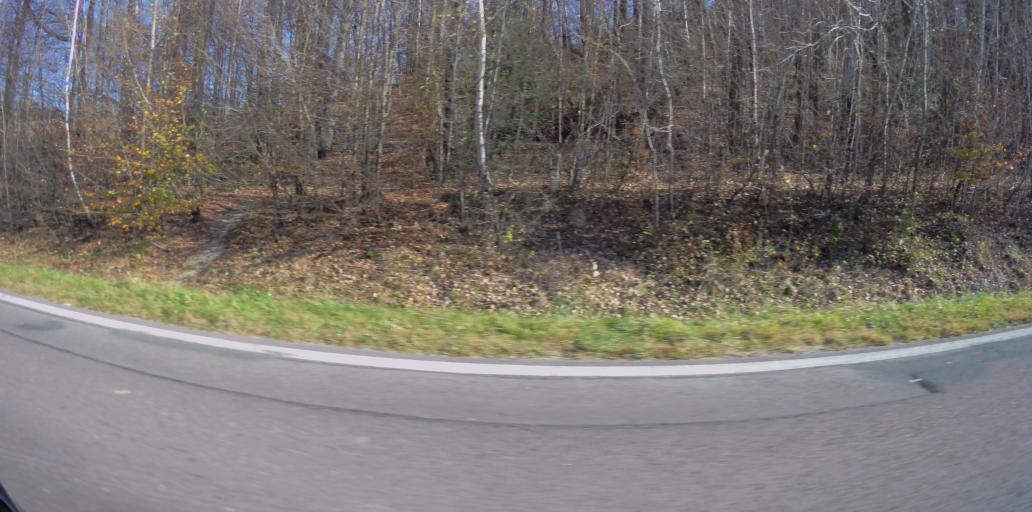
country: PL
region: Subcarpathian Voivodeship
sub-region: Powiat bieszczadzki
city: Ustrzyki Dolne
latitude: 49.5312
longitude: 22.6006
